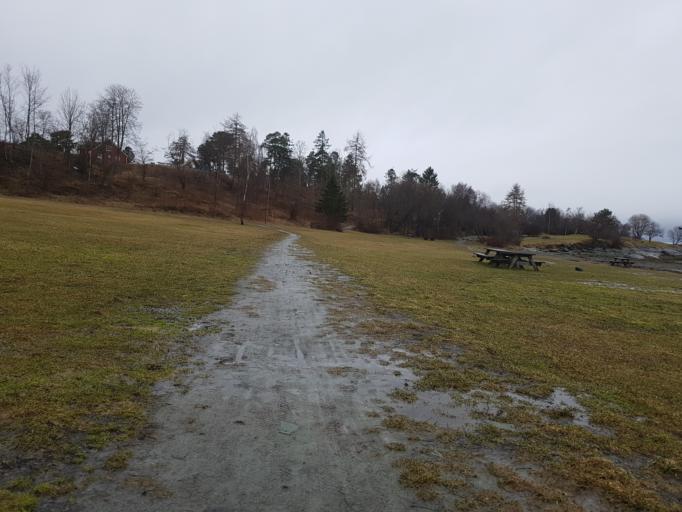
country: NO
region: Sor-Trondelag
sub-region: Trondheim
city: Trondheim
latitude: 63.4392
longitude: 10.4881
